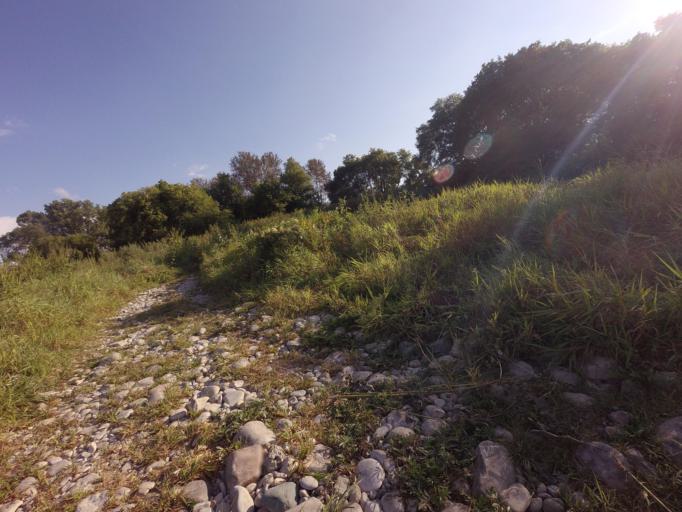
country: CA
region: Ontario
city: Goderich
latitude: 43.7517
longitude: -81.5729
